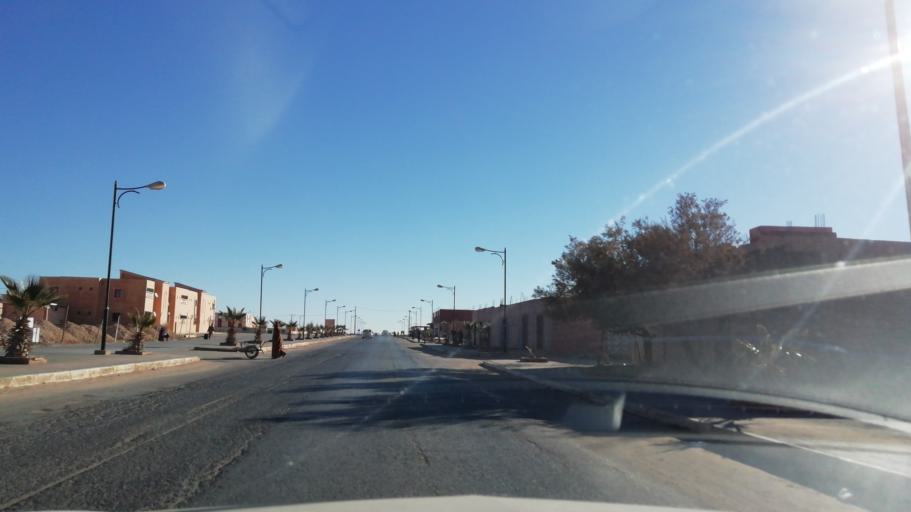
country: DZ
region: El Bayadh
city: El Bayadh
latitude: 33.8525
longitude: 0.6452
